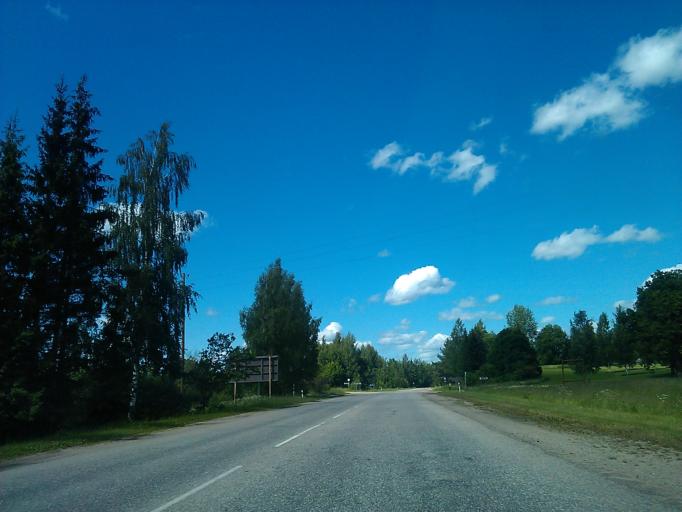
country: LV
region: Amatas Novads
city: Drabesi
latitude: 57.2340
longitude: 25.2535
